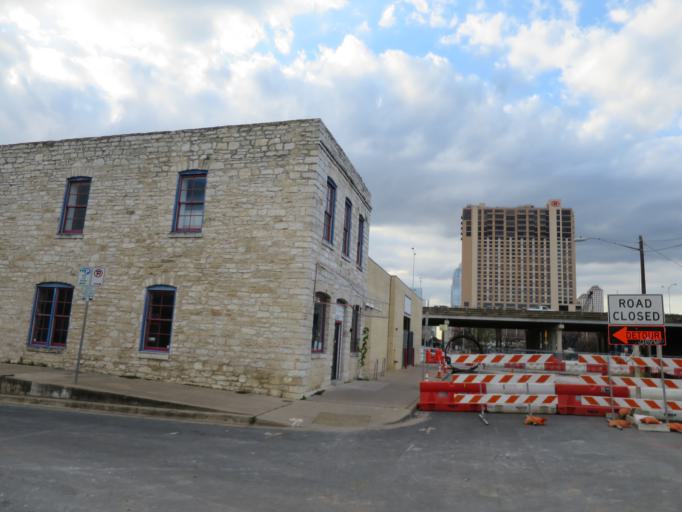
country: US
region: Texas
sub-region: Travis County
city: Austin
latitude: 30.2636
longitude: -97.7343
